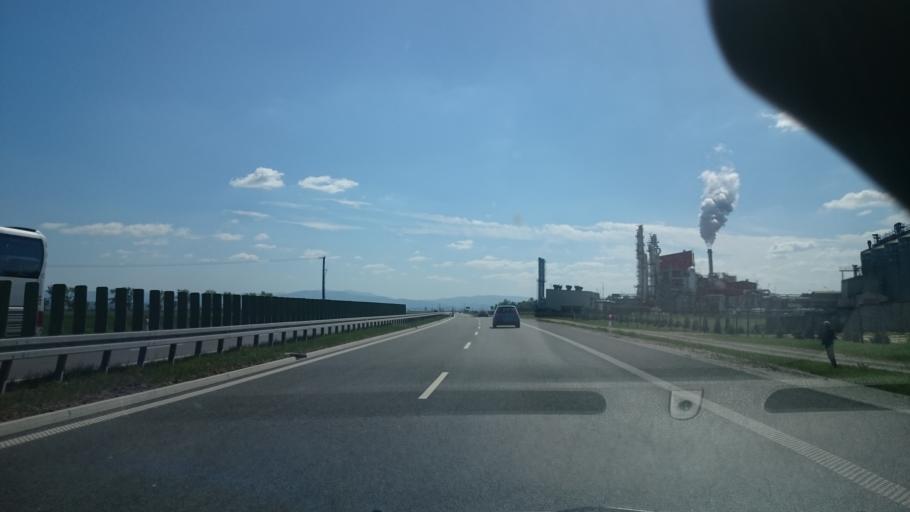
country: PL
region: Opole Voivodeship
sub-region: Powiat nyski
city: Nysa
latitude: 50.4826
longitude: 17.2671
